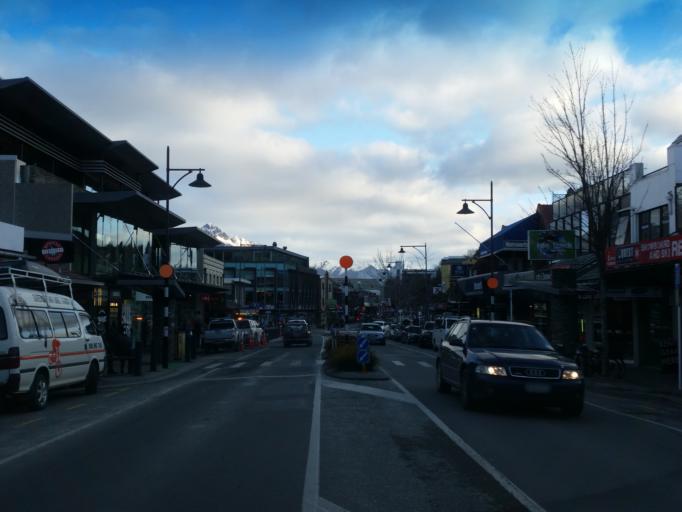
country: NZ
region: Otago
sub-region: Queenstown-Lakes District
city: Queenstown
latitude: -45.0312
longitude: 168.6599
